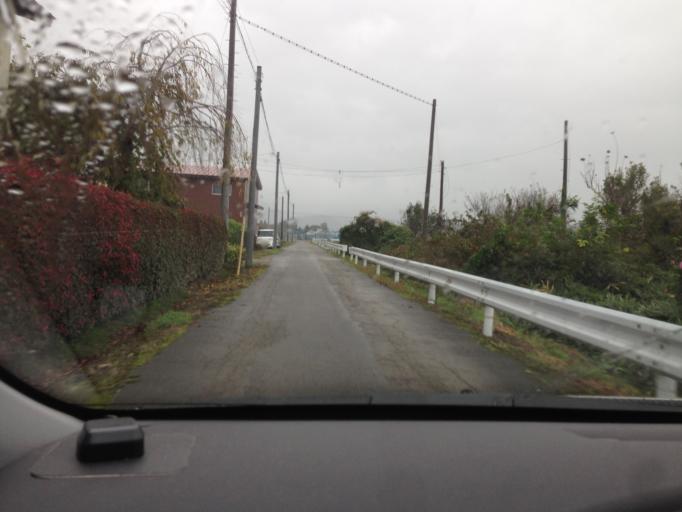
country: JP
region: Fukushima
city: Kitakata
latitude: 37.4618
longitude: 139.8724
